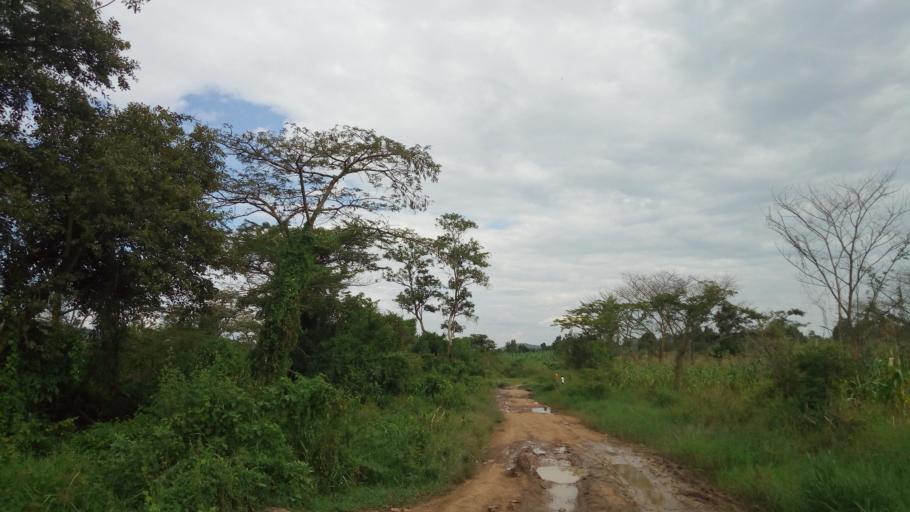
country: UG
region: Central Region
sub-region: Kiboga District
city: Kiboga
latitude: 0.7609
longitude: 31.6936
